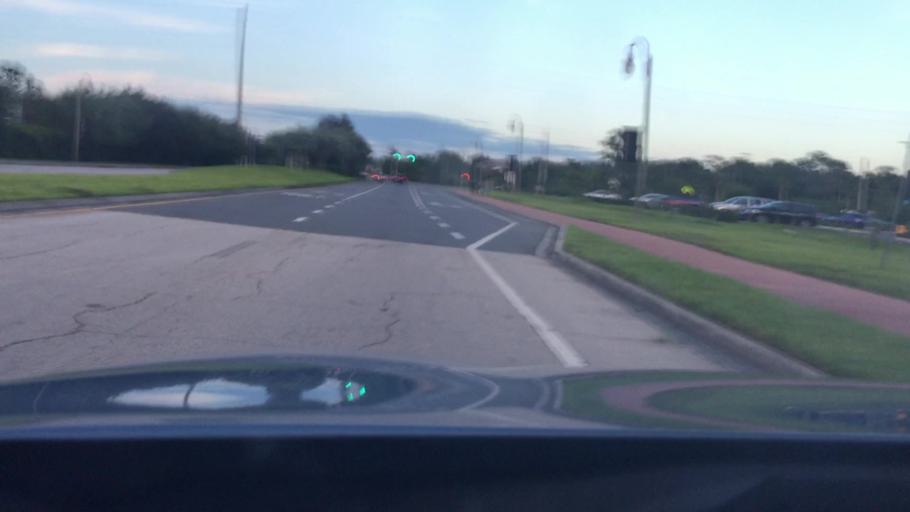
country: US
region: Florida
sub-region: Osceola County
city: Saint Cloud
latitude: 28.2240
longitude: -81.2949
